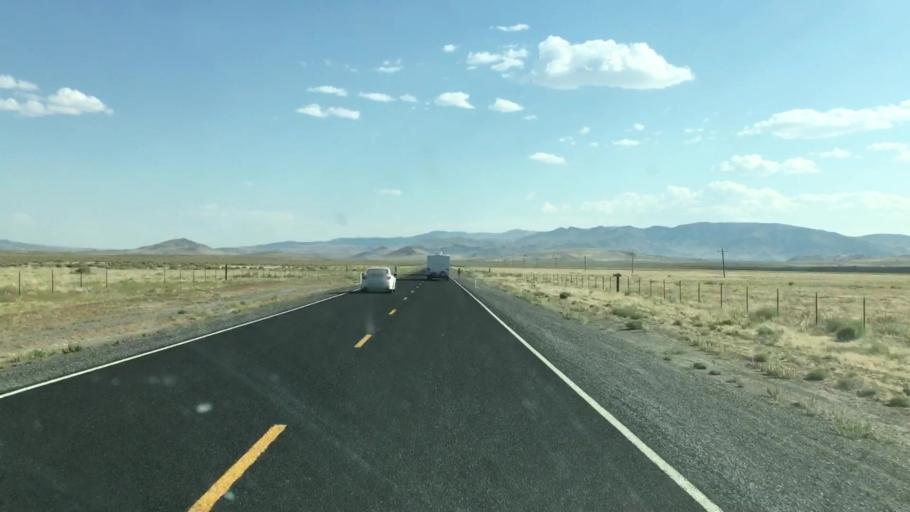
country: US
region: Nevada
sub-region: Lyon County
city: Fernley
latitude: 39.6810
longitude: -119.3346
